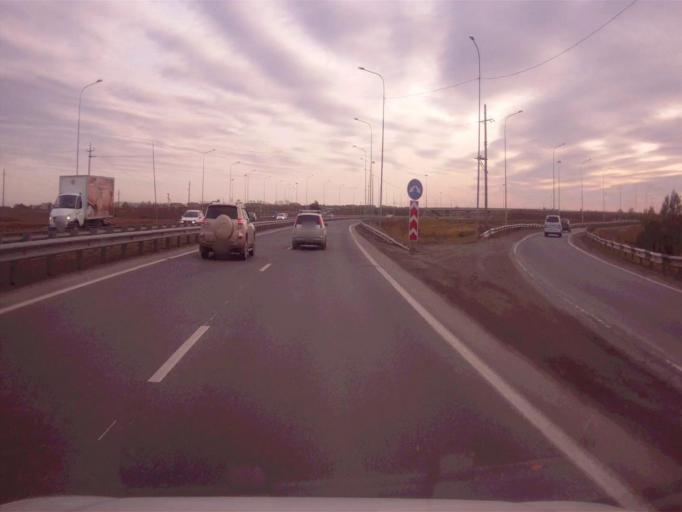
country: RU
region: Chelyabinsk
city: Novosineglazovskiy
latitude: 55.0067
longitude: 61.4531
